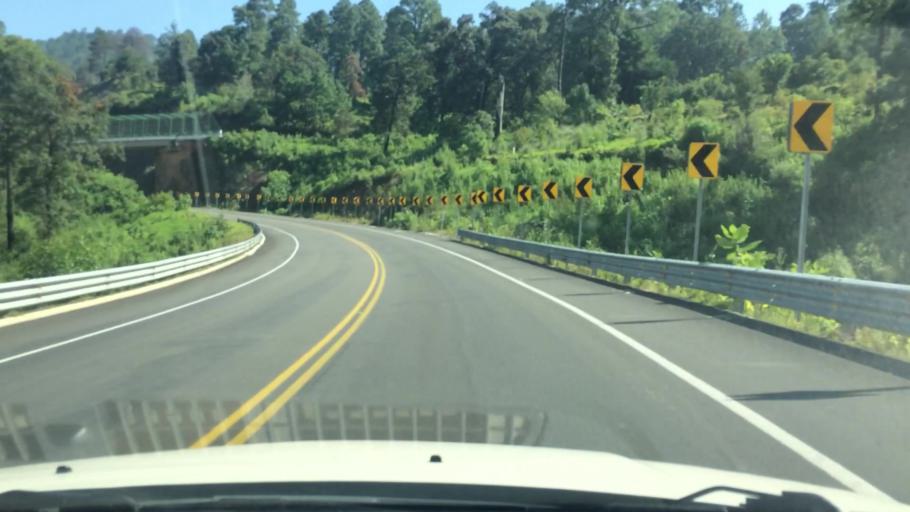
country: MX
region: Mexico
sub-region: Amanalco
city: Polvillos (San Bartolo Quinta Seccion)
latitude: 19.2286
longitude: -100.0738
